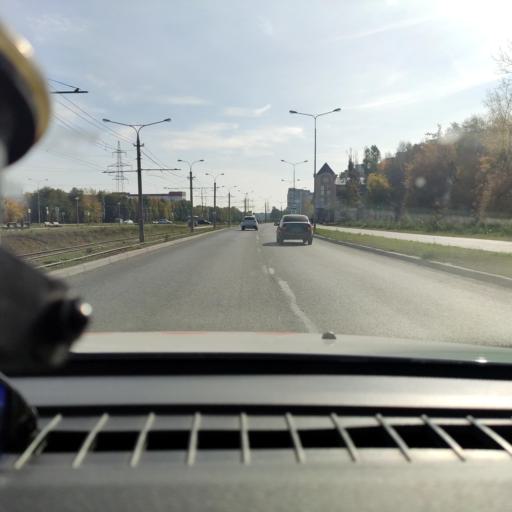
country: RU
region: Samara
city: Samara
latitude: 53.2589
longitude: 50.2421
